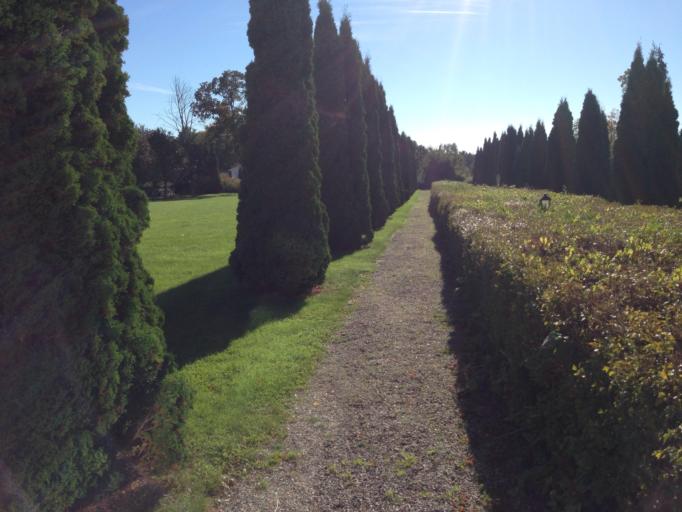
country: SE
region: Uppsala
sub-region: Enkopings Kommun
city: Enkoping
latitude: 59.6040
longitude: 17.0499
